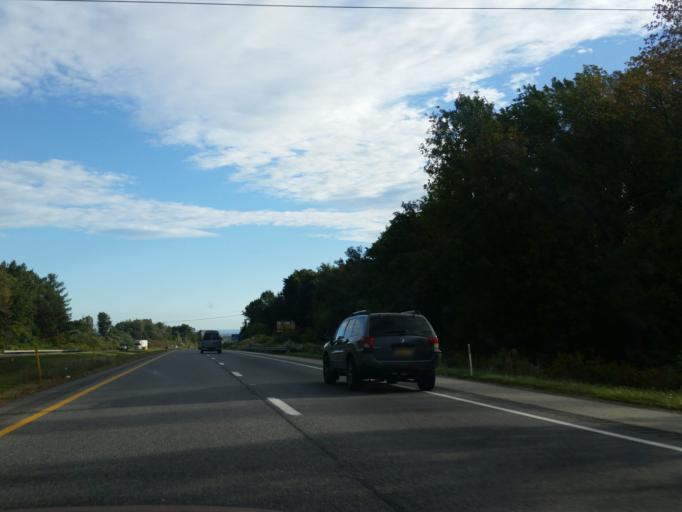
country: US
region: Pennsylvania
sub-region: Erie County
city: North East
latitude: 42.1788
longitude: -79.8406
